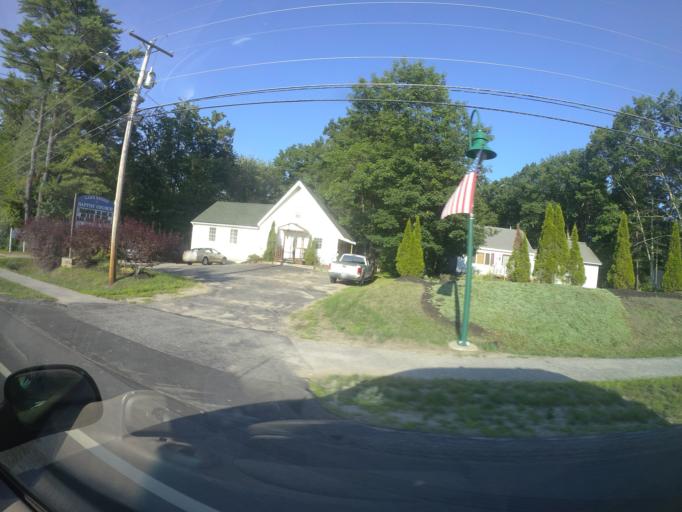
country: US
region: Maine
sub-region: Cumberland County
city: Raymond
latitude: 43.8858
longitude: -70.4649
